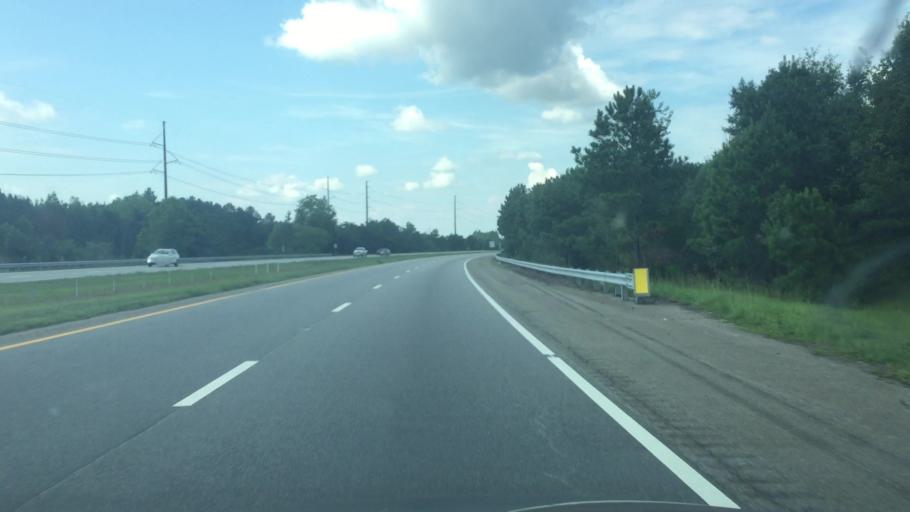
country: US
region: North Carolina
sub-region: Richmond County
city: Hamlet
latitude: 34.8580
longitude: -79.6838
